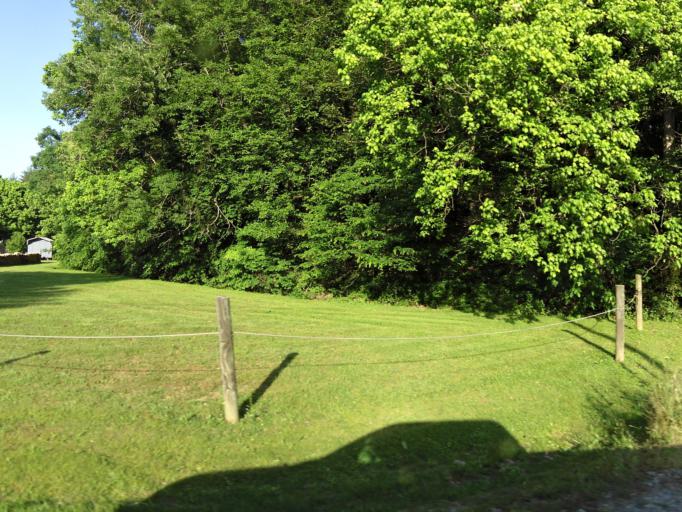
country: US
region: Tennessee
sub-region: Sevier County
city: Sevierville
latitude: 35.8424
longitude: -83.6221
